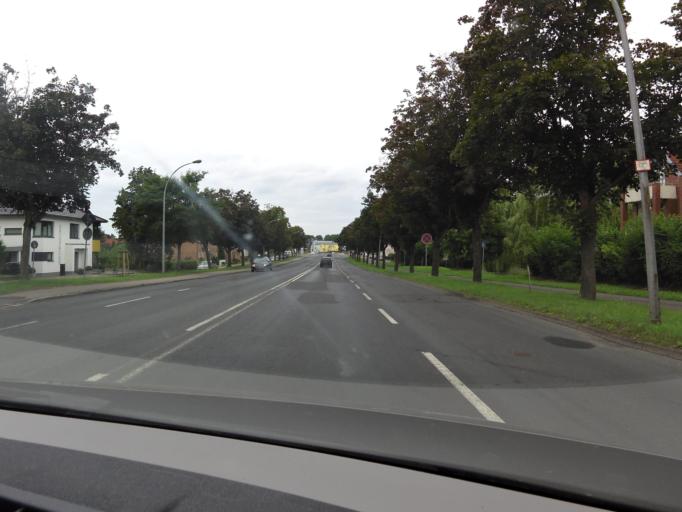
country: DE
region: Mecklenburg-Vorpommern
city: Neustrelitz
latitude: 53.3531
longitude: 13.0765
